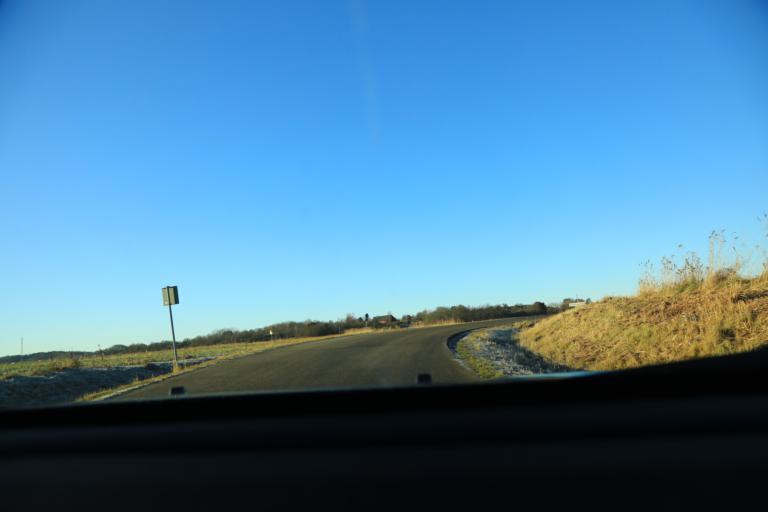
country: SE
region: Halland
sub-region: Varbergs Kommun
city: Varberg
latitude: 57.2059
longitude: 12.2210
